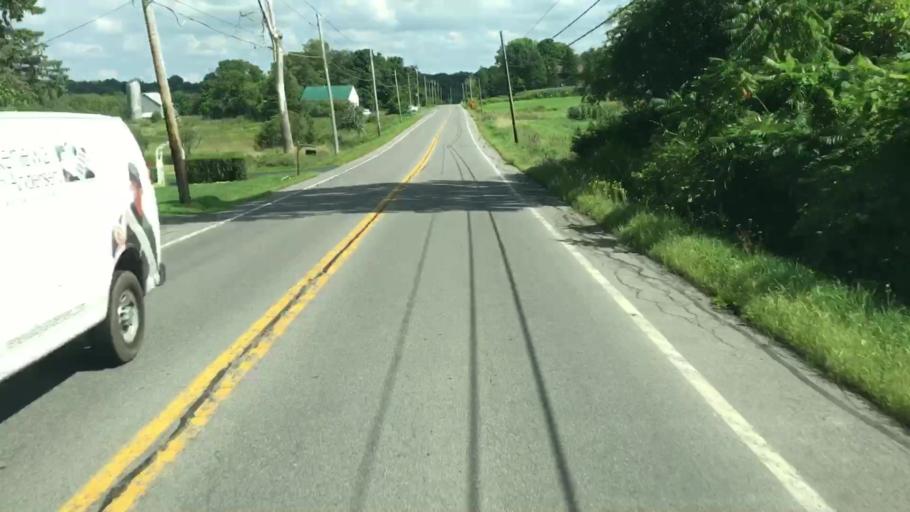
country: US
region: New York
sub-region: Onondaga County
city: Marcellus
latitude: 42.9840
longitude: -76.3035
